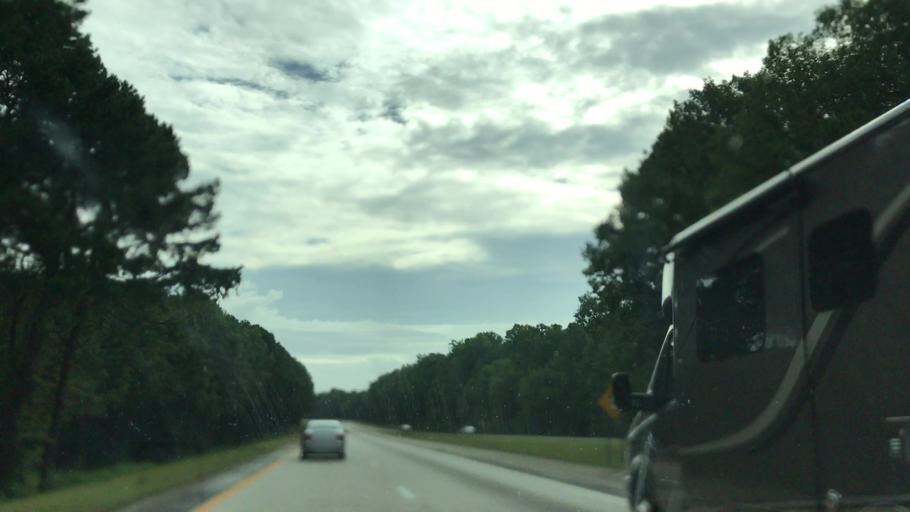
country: US
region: North Carolina
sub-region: Nash County
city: Red Oak
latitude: 36.0275
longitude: -77.8459
